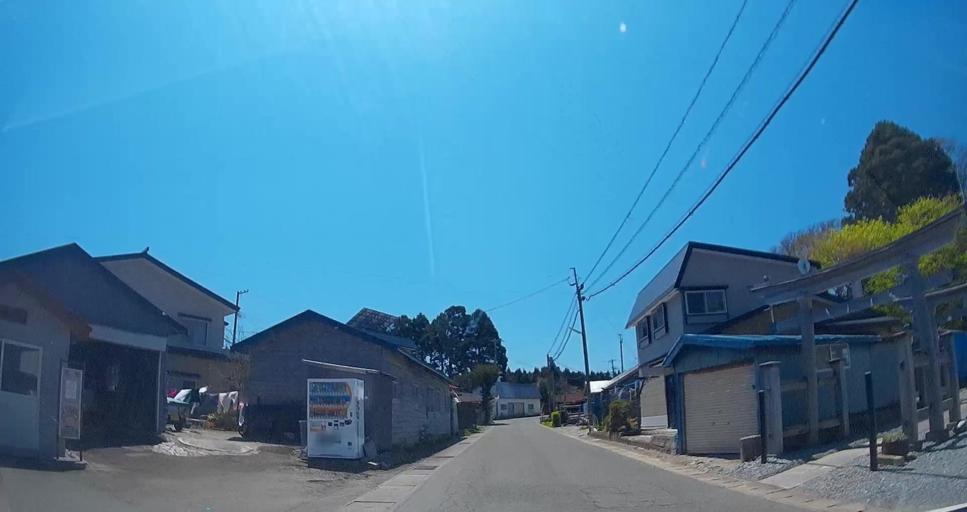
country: JP
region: Aomori
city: Mutsu
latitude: 41.3714
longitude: 141.4469
